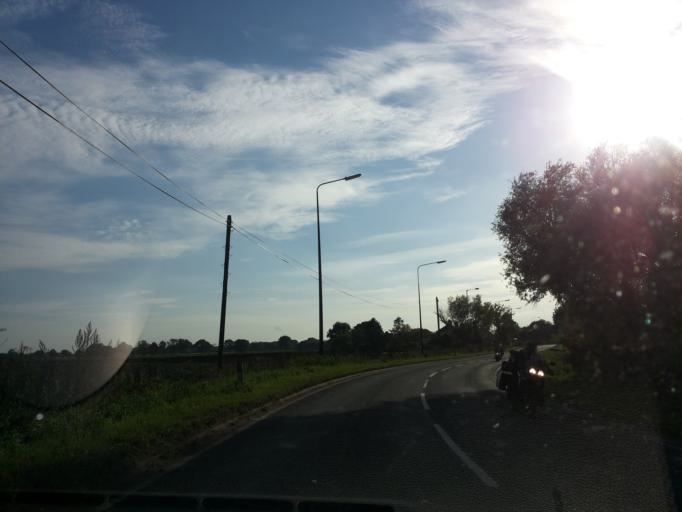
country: GB
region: England
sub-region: Doncaster
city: Hatfield
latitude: 53.5829
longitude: -0.9644
